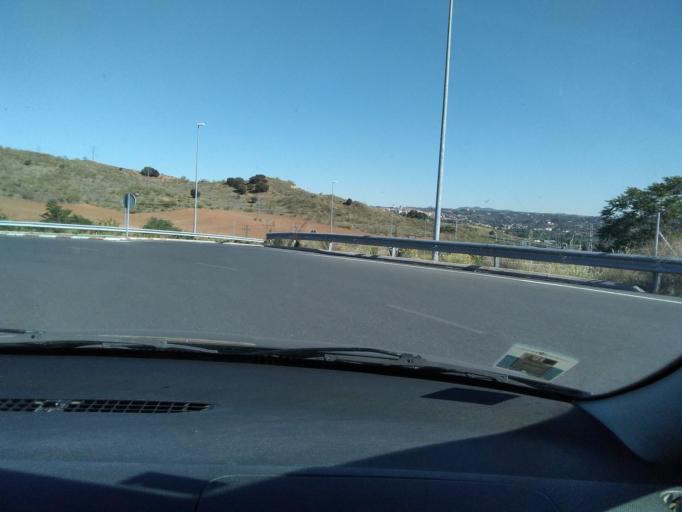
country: ES
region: Castille-La Mancha
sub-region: Province of Toledo
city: Toledo
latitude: 39.8878
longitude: -4.0554
